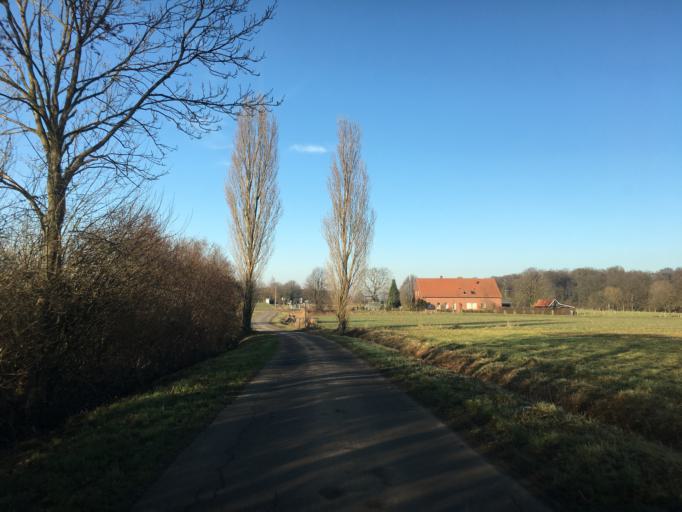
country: DE
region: North Rhine-Westphalia
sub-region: Regierungsbezirk Munster
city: Altenberge
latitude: 52.0346
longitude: 7.5385
